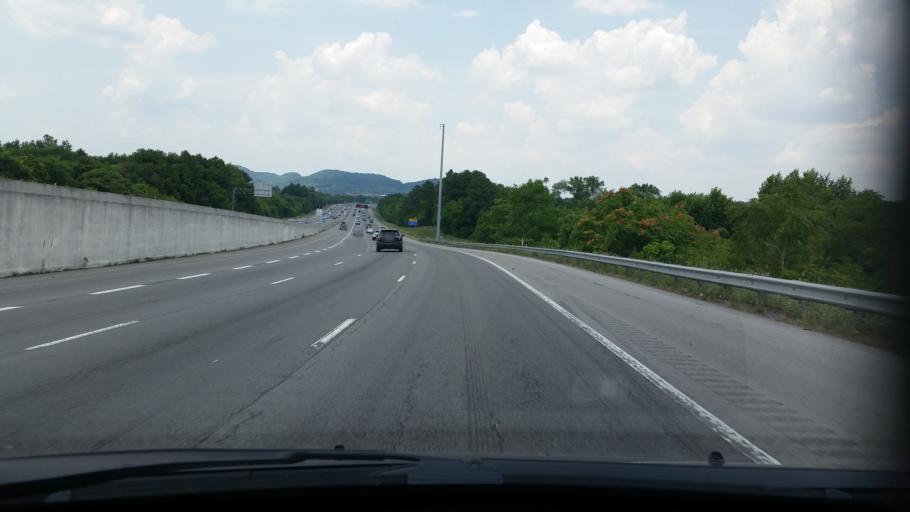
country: US
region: Tennessee
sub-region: Williamson County
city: Brentwood Estates
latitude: 36.0121
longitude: -86.7848
